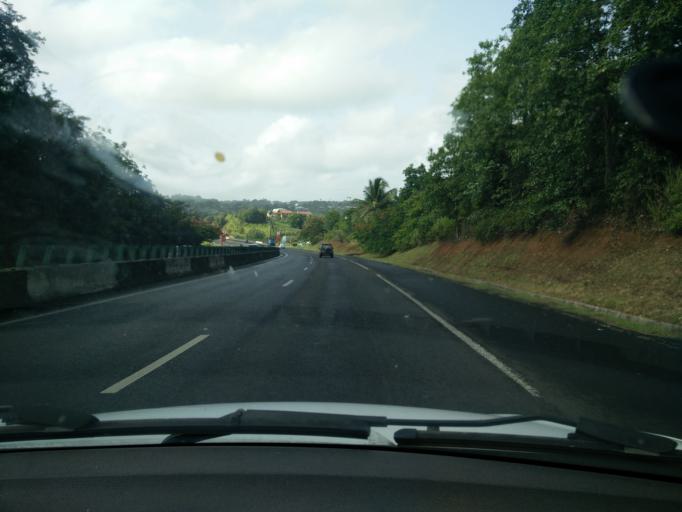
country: GP
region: Guadeloupe
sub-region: Guadeloupe
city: Petit-Bourg
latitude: 16.1897
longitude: -61.6077
